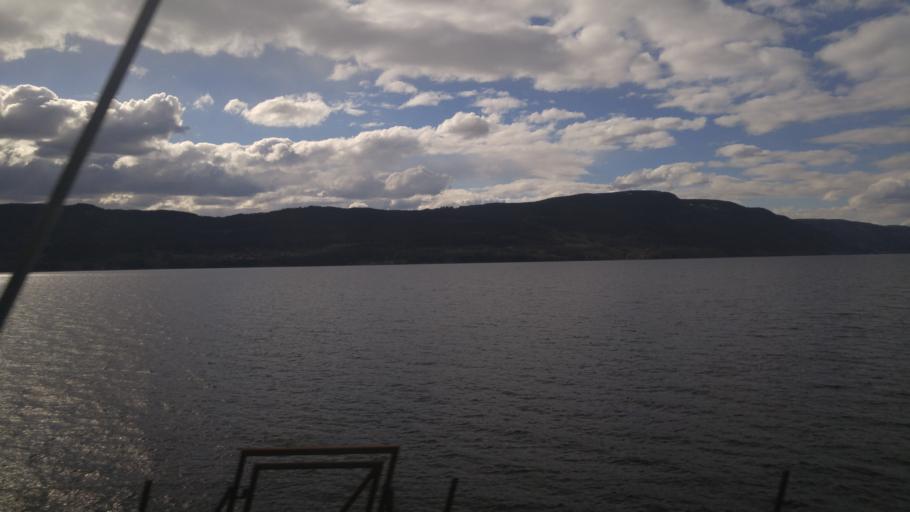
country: NO
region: Hedmark
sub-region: Stange
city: Stange
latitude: 60.5405
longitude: 11.2443
